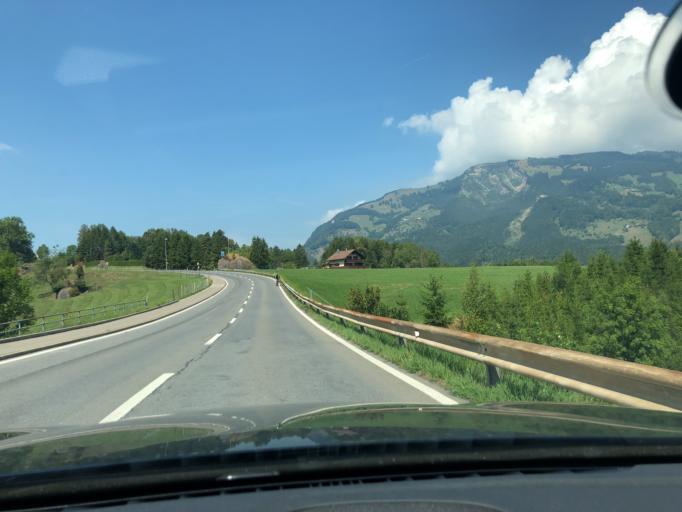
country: CH
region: Schwyz
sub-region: Bezirk Schwyz
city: Goldau
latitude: 47.0380
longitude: 8.5620
